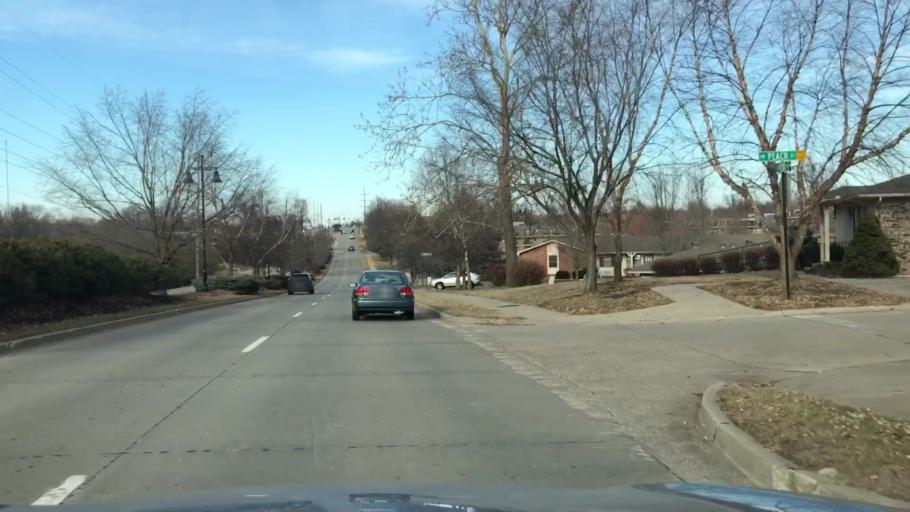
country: US
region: Missouri
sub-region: Jackson County
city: Lees Summit
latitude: 38.9210
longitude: -94.4129
